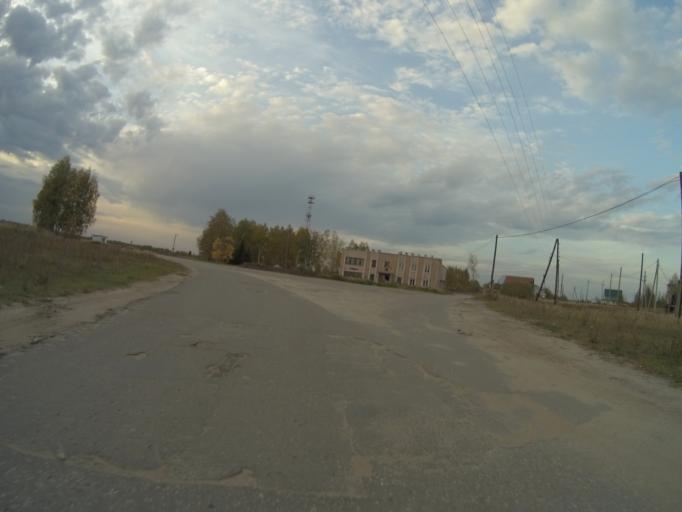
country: RU
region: Vladimir
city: Sobinka
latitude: 55.8755
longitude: 40.0989
